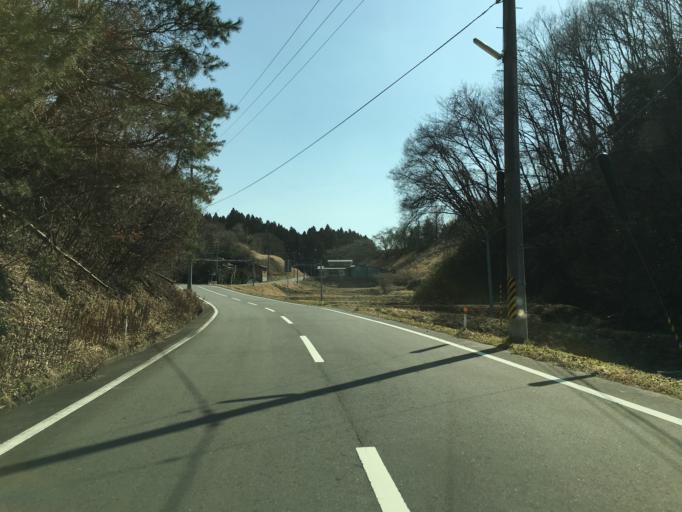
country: JP
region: Fukushima
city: Ishikawa
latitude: 37.0982
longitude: 140.4427
